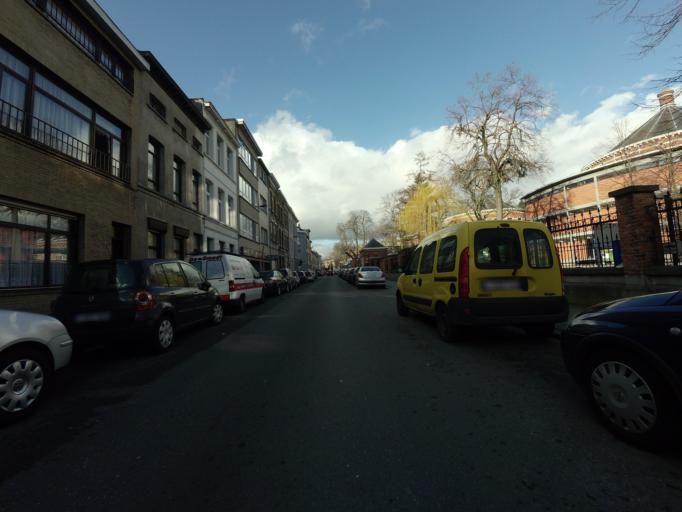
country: BE
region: Flanders
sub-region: Provincie Antwerpen
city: Antwerpen
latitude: 51.2223
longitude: 4.4337
